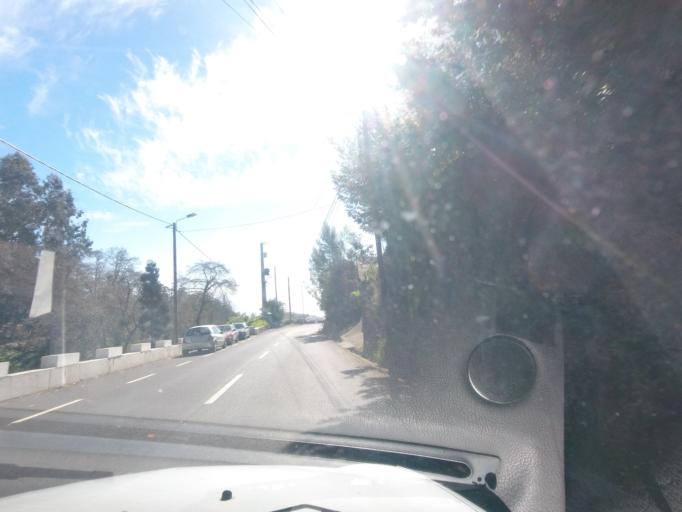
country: PT
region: Madeira
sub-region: Camara de Lobos
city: Curral das Freiras
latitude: 32.6879
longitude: -16.9542
